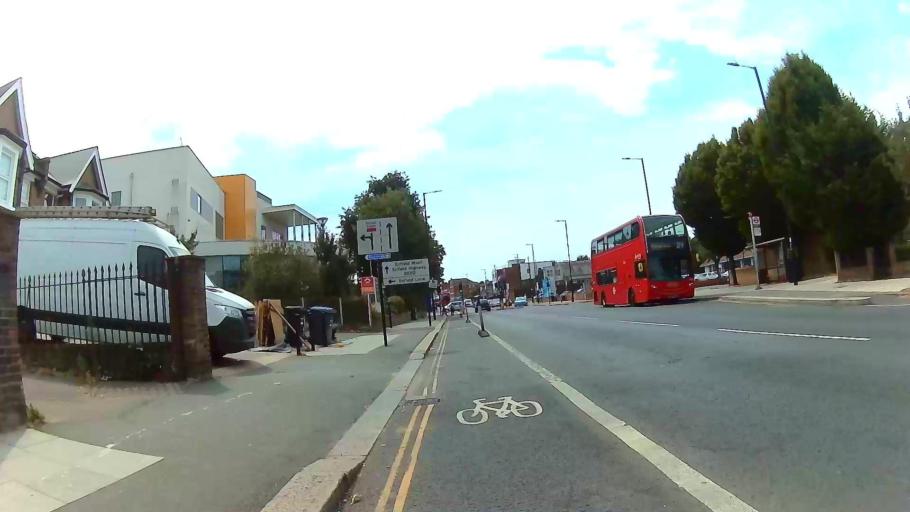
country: GB
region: England
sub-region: Hertfordshire
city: Waltham Cross
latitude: 51.6725
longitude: -0.0394
